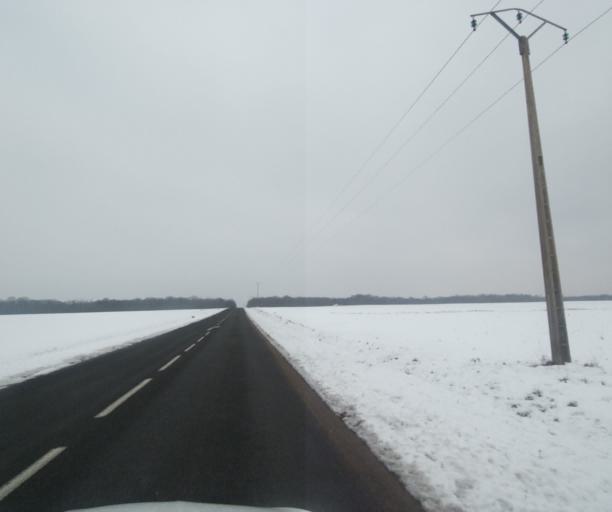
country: FR
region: Champagne-Ardenne
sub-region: Departement de la Haute-Marne
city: Villiers-en-Lieu
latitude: 48.6042
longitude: 4.8796
